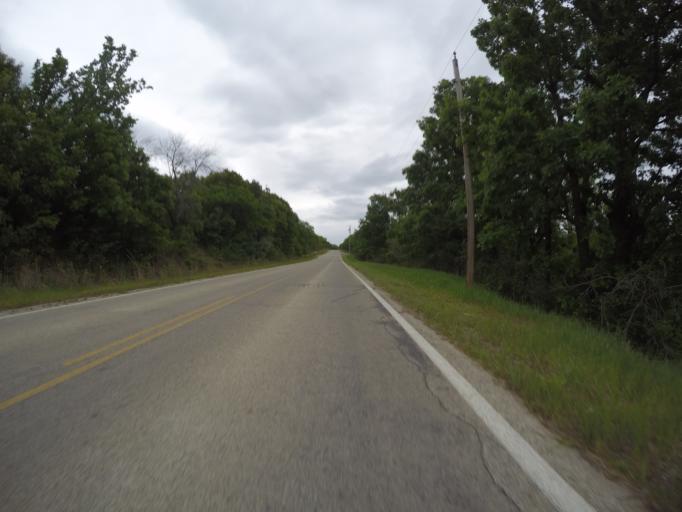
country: US
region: Kansas
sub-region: Pottawatomie County
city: Wamego
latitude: 39.1849
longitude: -96.4086
